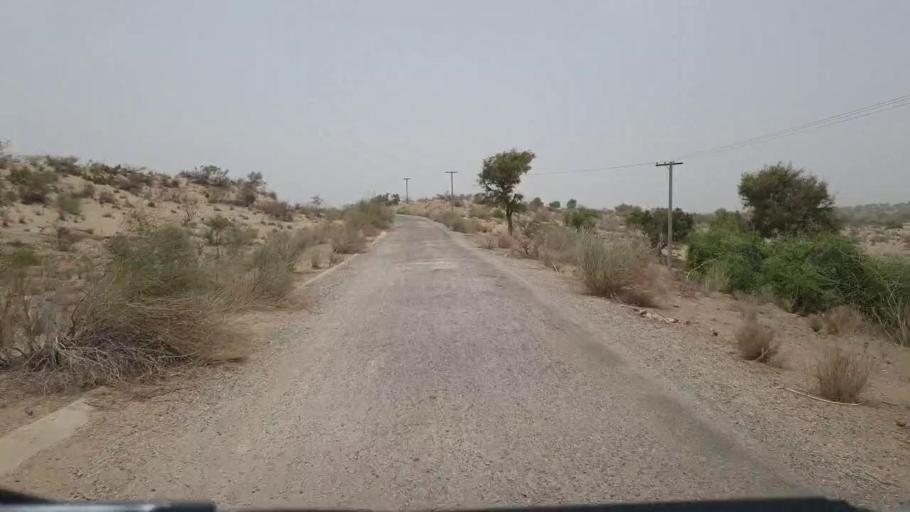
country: PK
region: Sindh
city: Naukot
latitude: 24.7545
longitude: 69.5524
